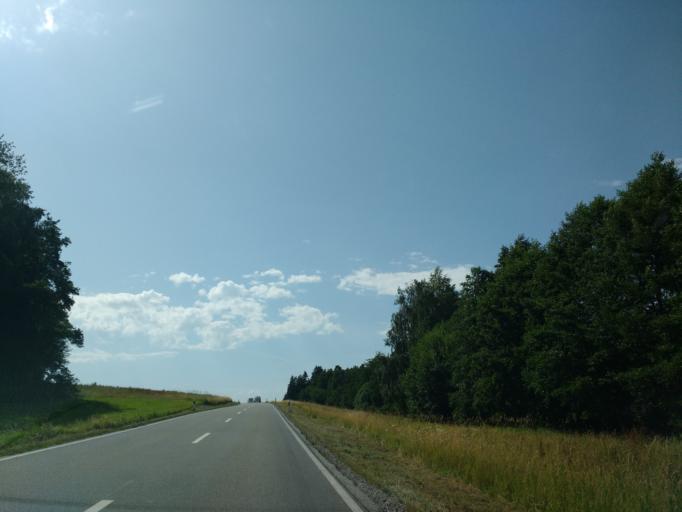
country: DE
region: Bavaria
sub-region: Upper Bavaria
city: Kienberg
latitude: 48.0434
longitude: 12.4434
